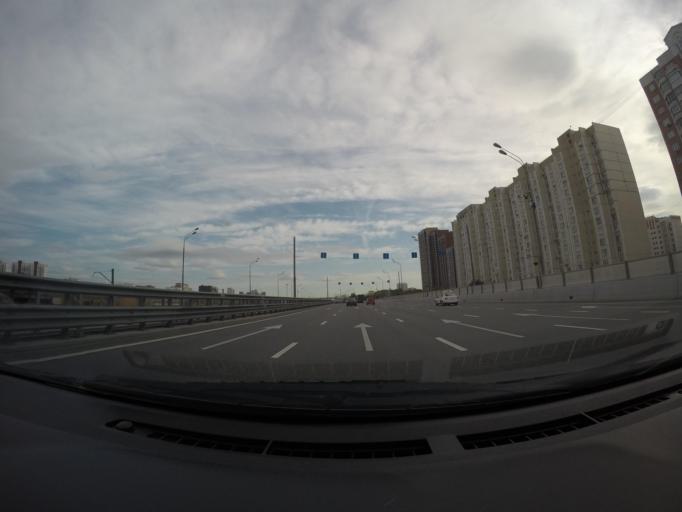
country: RU
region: Moscow
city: Novokhovrino
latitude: 55.8719
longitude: 37.5012
